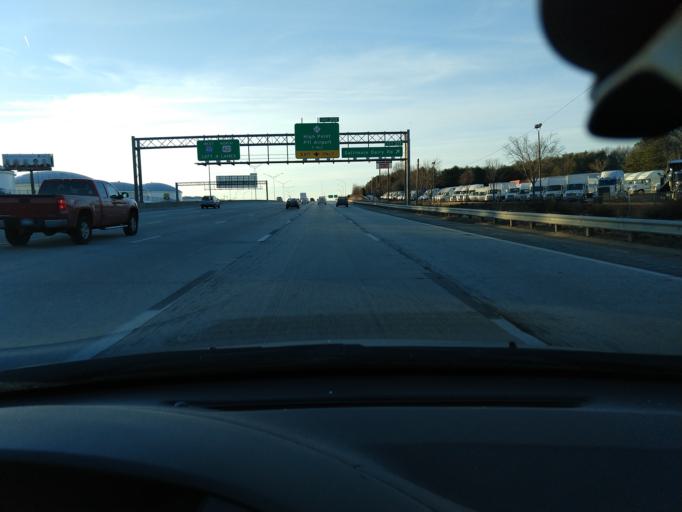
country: US
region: North Carolina
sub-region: Guilford County
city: Jamestown
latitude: 36.0729
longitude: -79.9352
